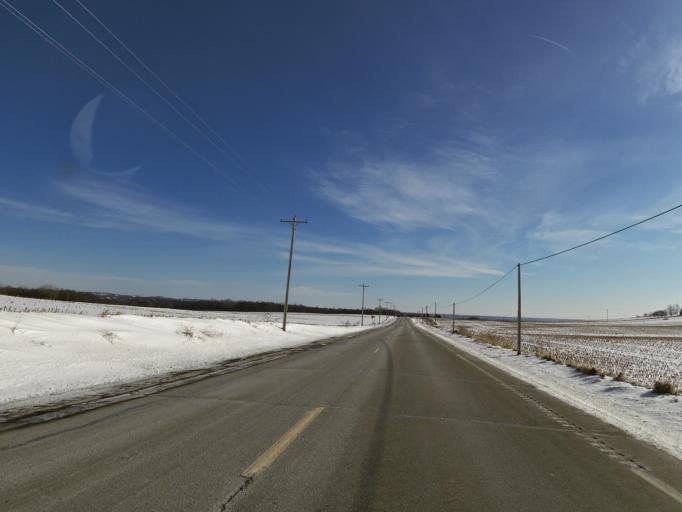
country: US
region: Minnesota
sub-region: Dakota County
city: Hastings
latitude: 44.7566
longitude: -92.9093
